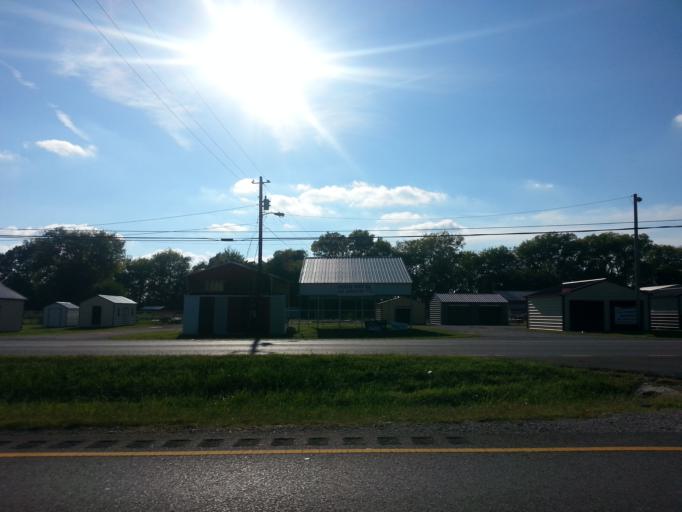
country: US
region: Alabama
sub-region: Colbert County
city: Muscle Shoals
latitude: 34.7186
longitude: -87.6678
